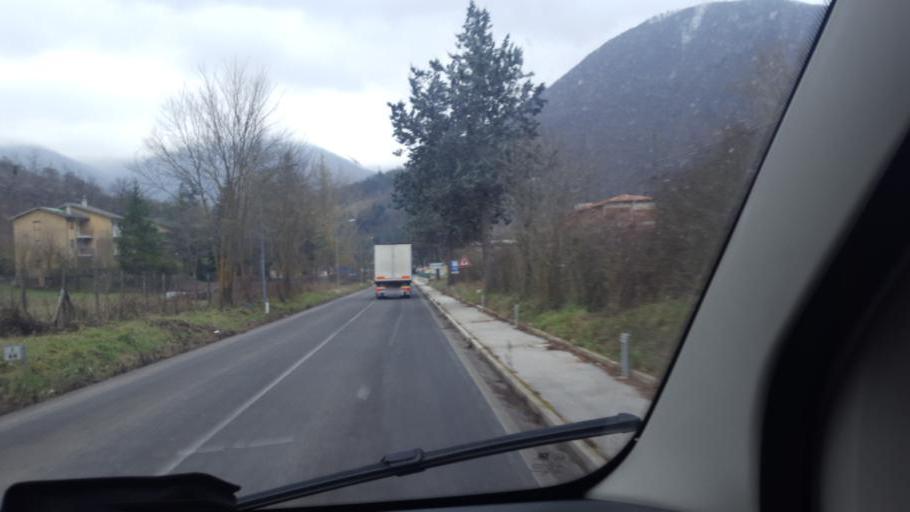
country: IT
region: The Marches
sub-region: Provincia di Macerata
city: Visso
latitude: 42.9367
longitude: 13.0820
